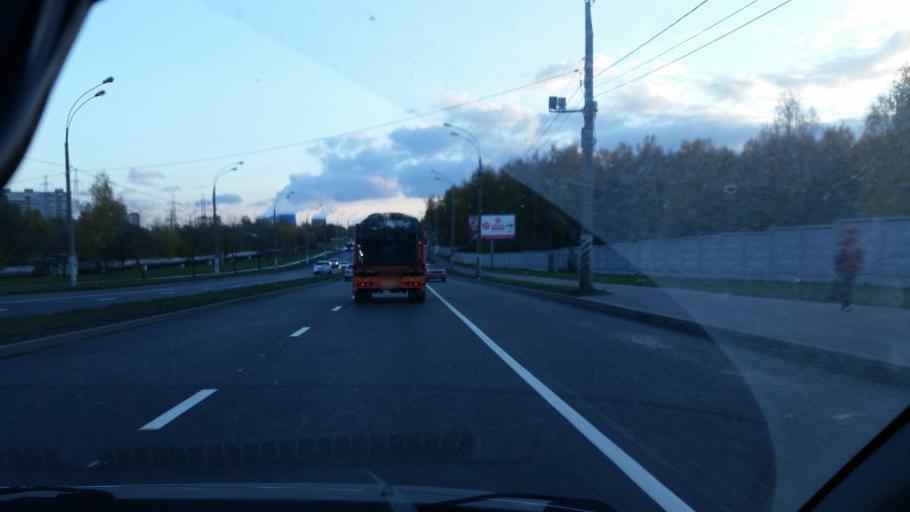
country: RU
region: Moskovskaya
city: Biryulevo Zapadnoye
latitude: 55.5963
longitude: 37.6360
